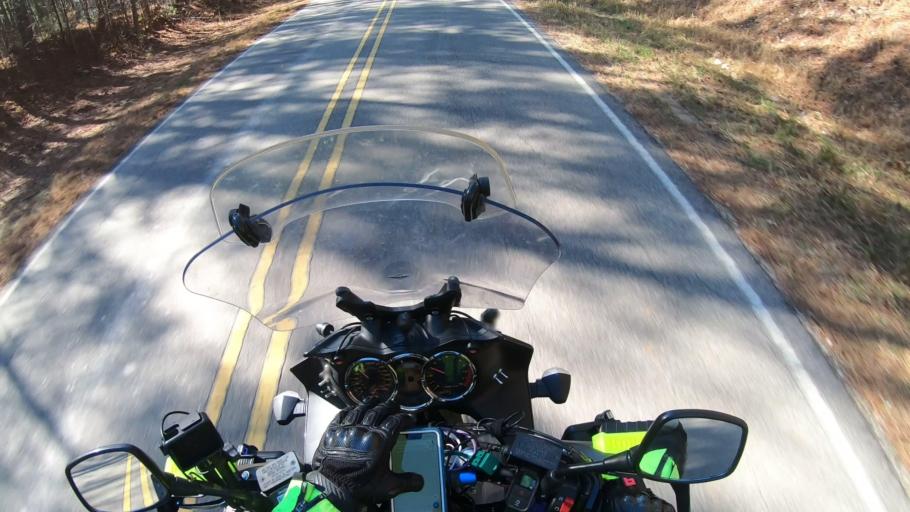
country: US
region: Alabama
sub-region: Clay County
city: Ashland
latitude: 33.3702
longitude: -85.8933
